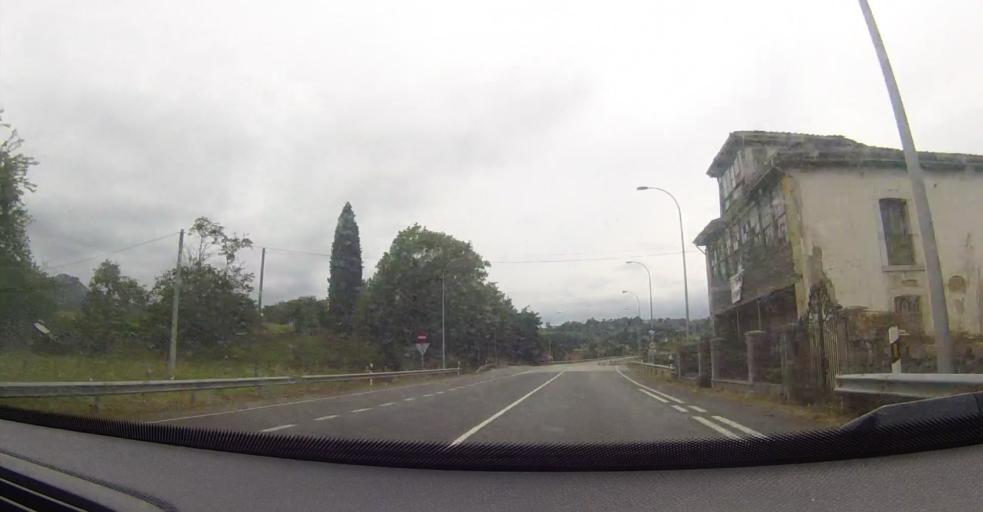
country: ES
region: Asturias
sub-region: Province of Asturias
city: Pilona
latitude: 43.3467
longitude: -5.3516
